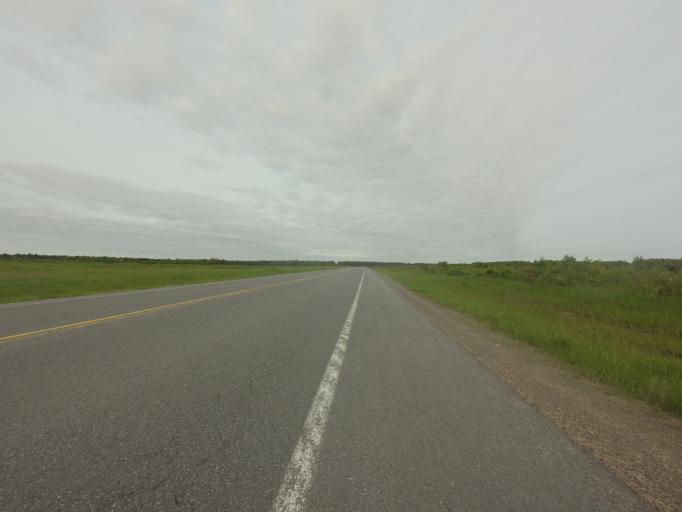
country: US
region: New York
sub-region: Jefferson County
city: Carthage
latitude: 44.0343
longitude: -75.6319
